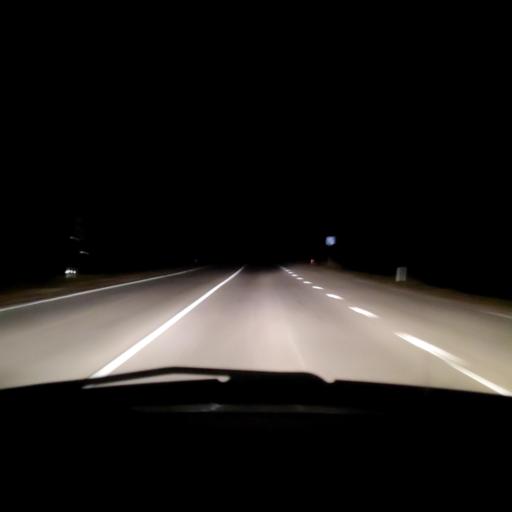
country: RU
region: Bashkortostan
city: Iglino
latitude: 54.9564
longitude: 56.4813
